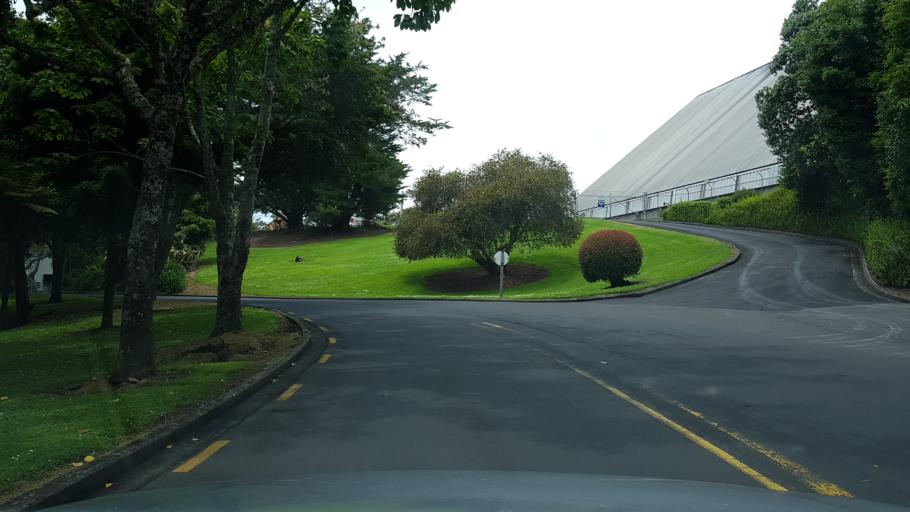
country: NZ
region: Auckland
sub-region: Auckland
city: North Shore
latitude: -36.8206
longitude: 174.7208
